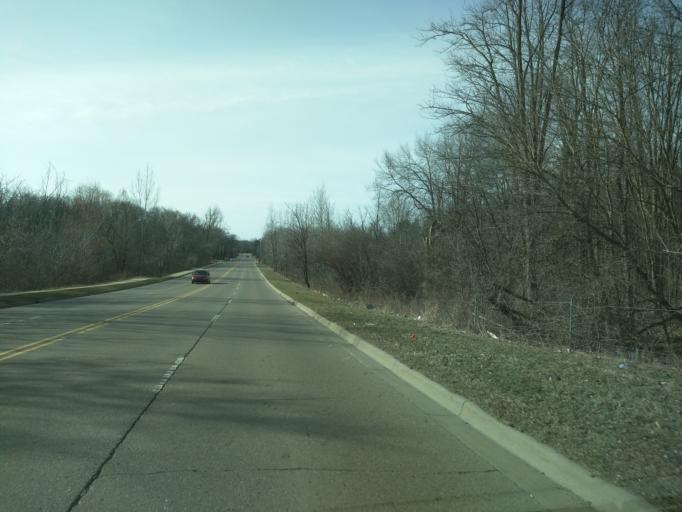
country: US
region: Michigan
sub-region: Ingham County
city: Haslett
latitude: 42.7689
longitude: -84.4131
